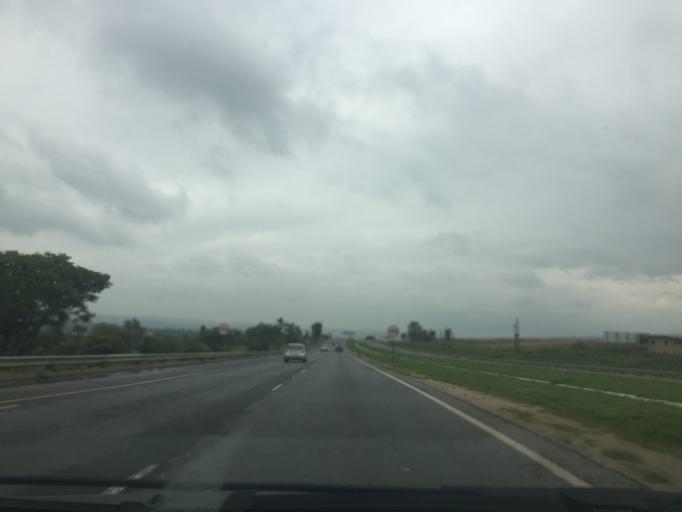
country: ZA
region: Gauteng
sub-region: City of Johannesburg Metropolitan Municipality
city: Diepsloot
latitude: -25.9522
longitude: 27.9125
